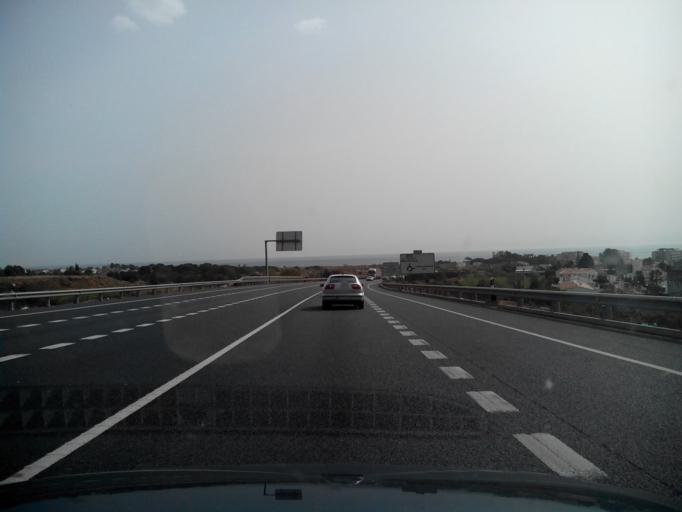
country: ES
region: Catalonia
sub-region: Provincia de Tarragona
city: Creixell
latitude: 41.1594
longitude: 1.4205
